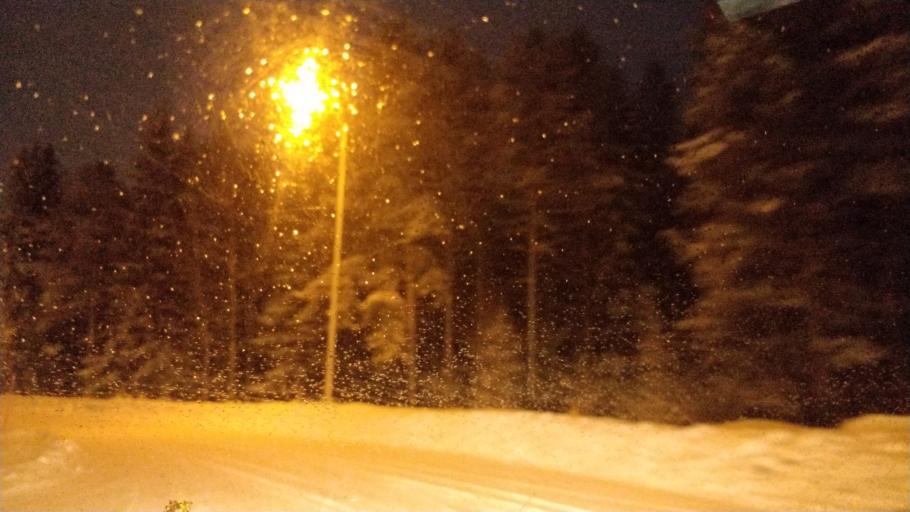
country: FI
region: Northern Ostrobothnia
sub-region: Oulu
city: Haukipudas
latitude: 65.1302
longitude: 25.4303
